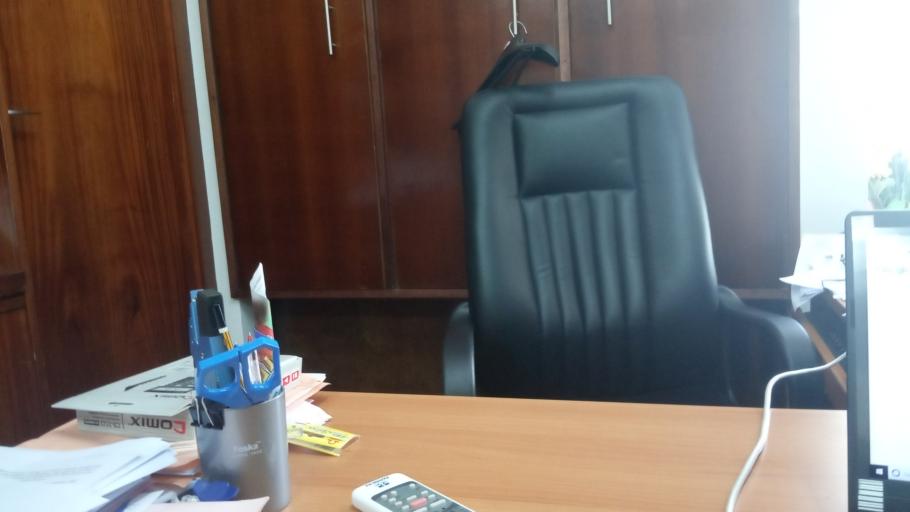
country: CI
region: Lagunes
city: Abidjan
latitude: 5.3199
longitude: -4.0176
